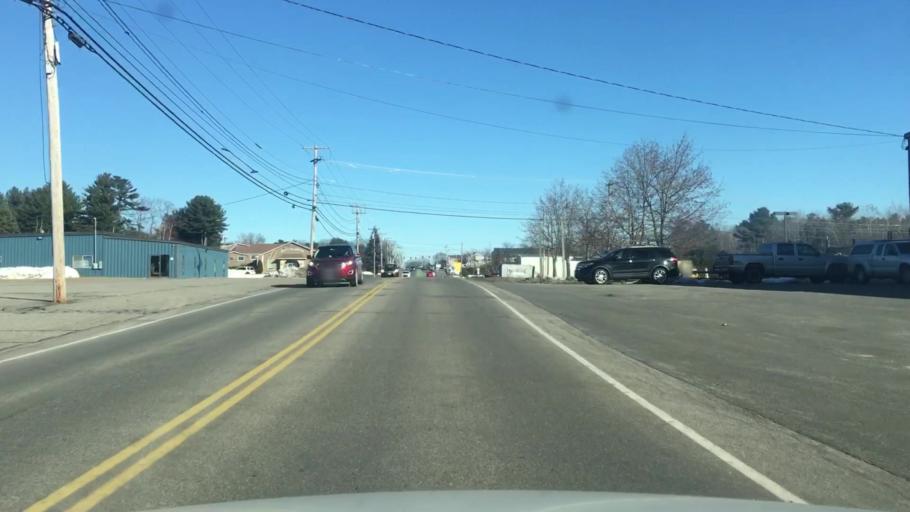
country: US
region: Maine
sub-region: York County
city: Biddeford
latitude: 43.4661
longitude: -70.4882
